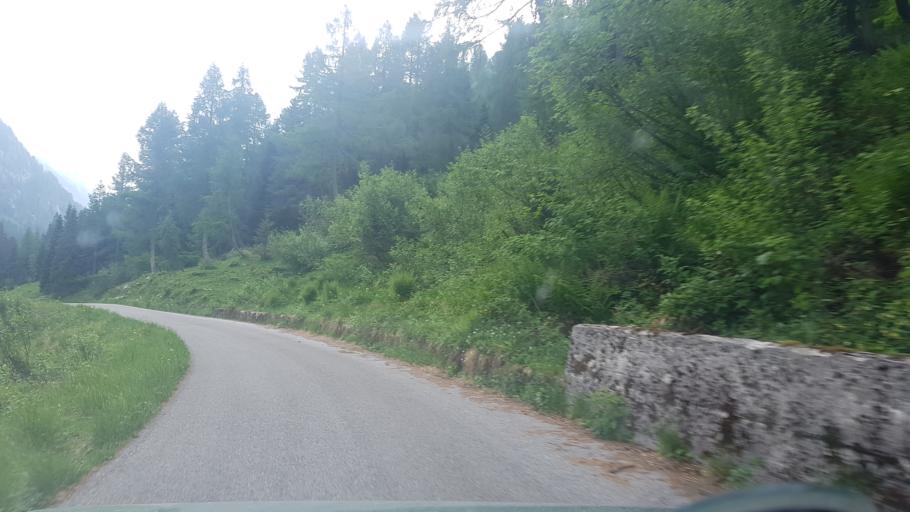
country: IT
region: Friuli Venezia Giulia
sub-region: Provincia di Udine
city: Paularo
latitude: 46.5609
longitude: 13.1783
